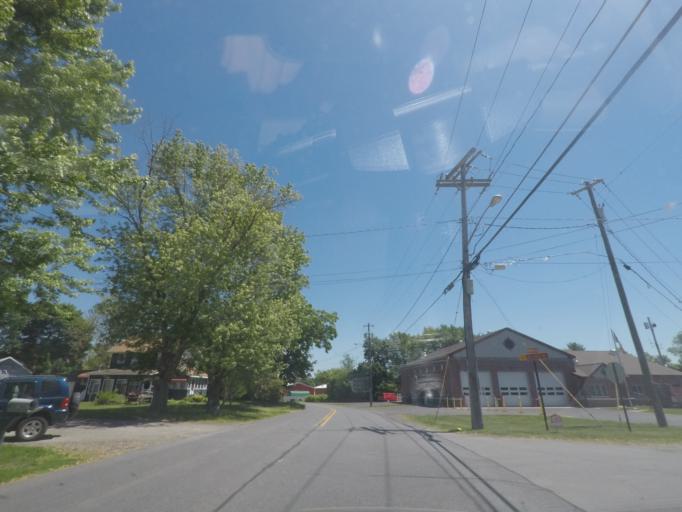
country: US
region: New York
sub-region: Saratoga County
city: Stillwater
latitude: 42.9363
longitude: -73.6639
